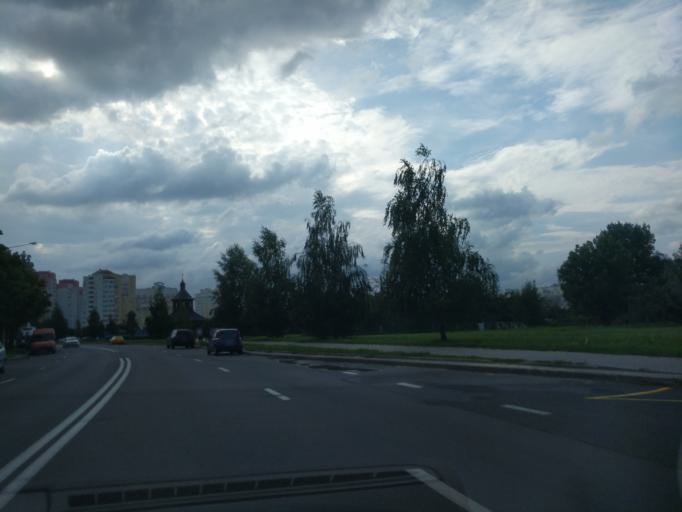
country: BY
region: Minsk
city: Malinovka
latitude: 53.8520
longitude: 27.4613
